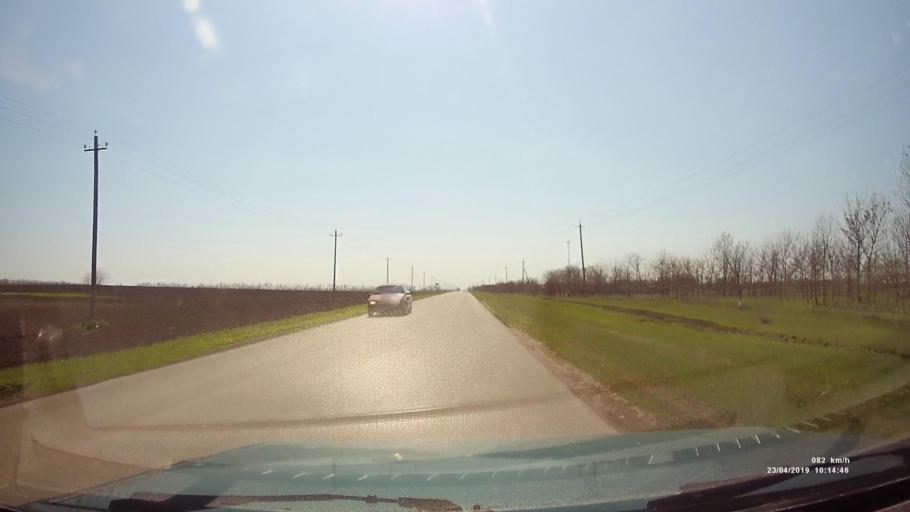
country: RU
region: Rostov
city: Sovetskoye
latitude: 46.6738
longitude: 42.3737
